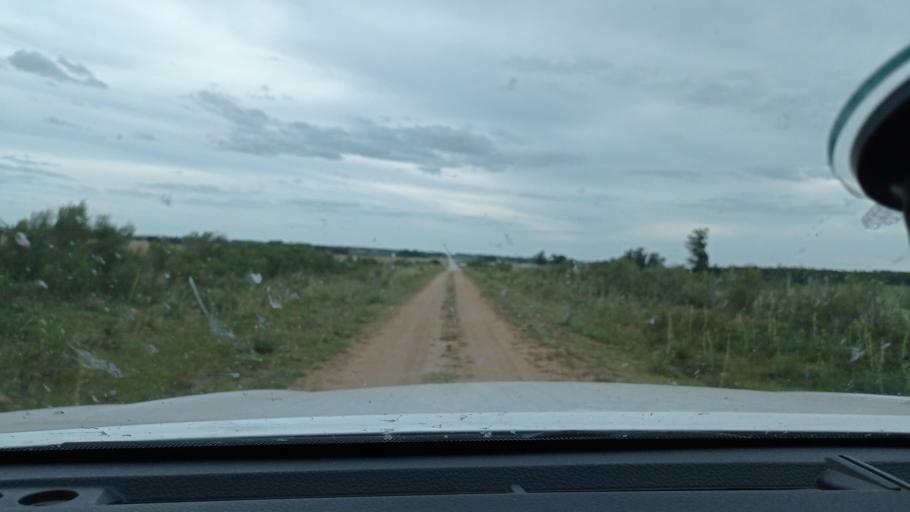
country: UY
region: Florida
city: Casupa
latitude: -34.1314
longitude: -55.8011
